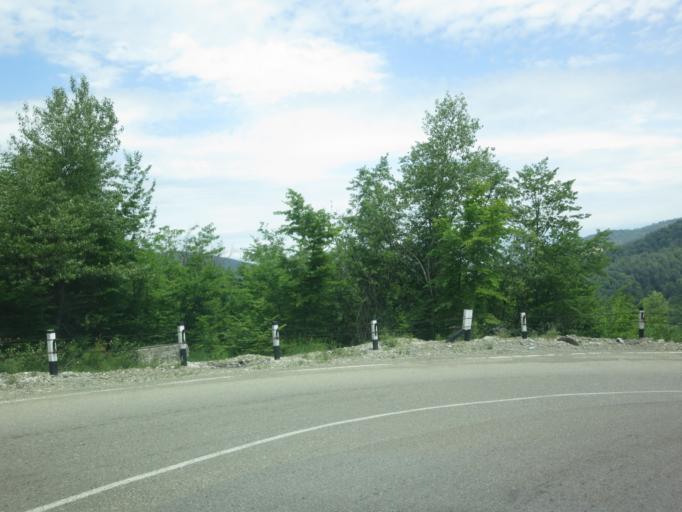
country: GE
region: Kakheti
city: Sagarejo
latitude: 41.8670
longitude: 45.3472
